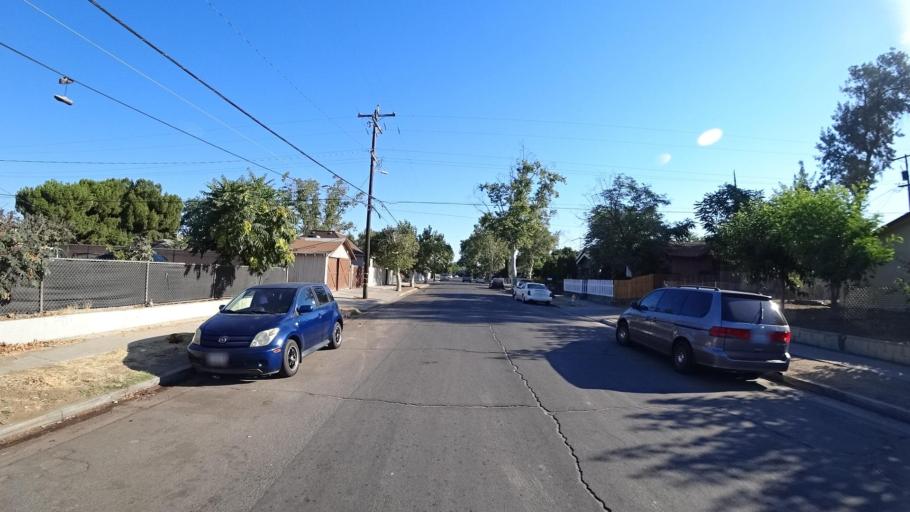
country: US
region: California
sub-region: Fresno County
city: Fresno
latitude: 36.7481
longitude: -119.7793
